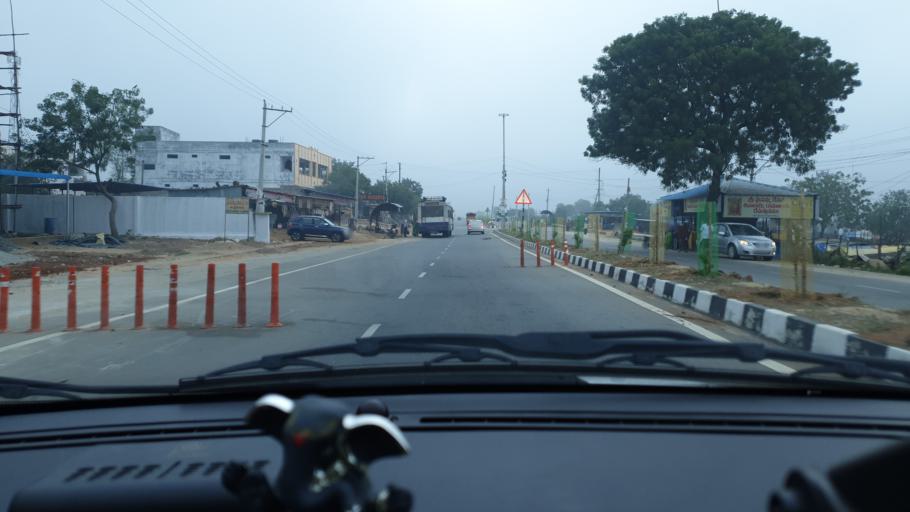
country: IN
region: Telangana
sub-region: Mahbubnagar
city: Farrukhnagar
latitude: 16.9548
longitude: 78.5168
